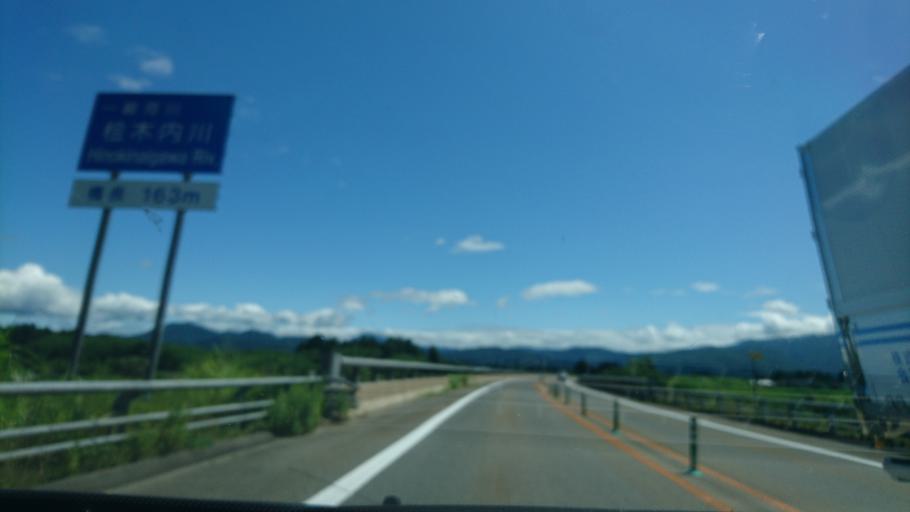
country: JP
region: Akita
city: Kakunodatemachi
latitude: 39.6111
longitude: 140.5601
